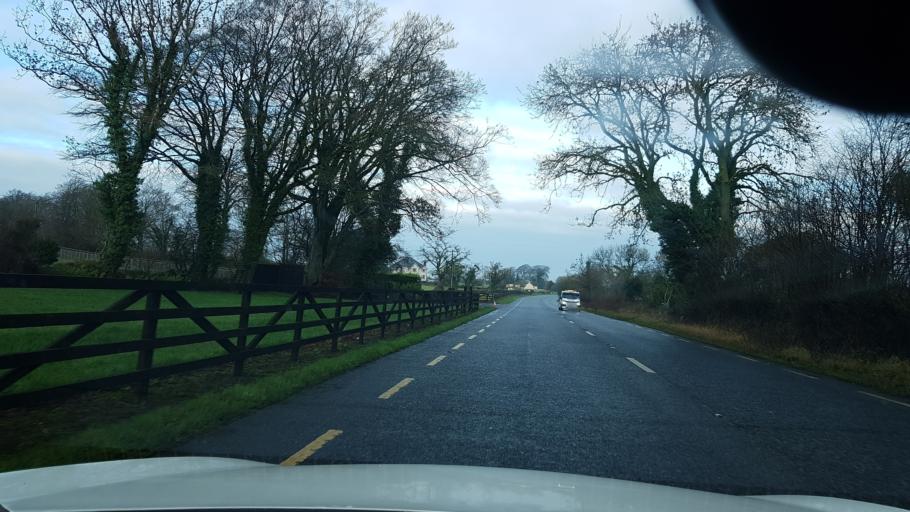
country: IE
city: Kentstown
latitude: 53.5767
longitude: -6.5849
